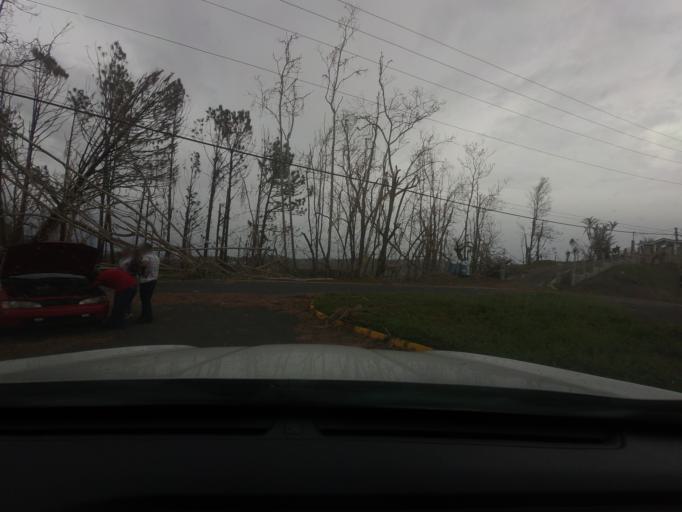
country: PR
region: Ciales
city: Ciales
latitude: 18.2721
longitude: -66.4814
